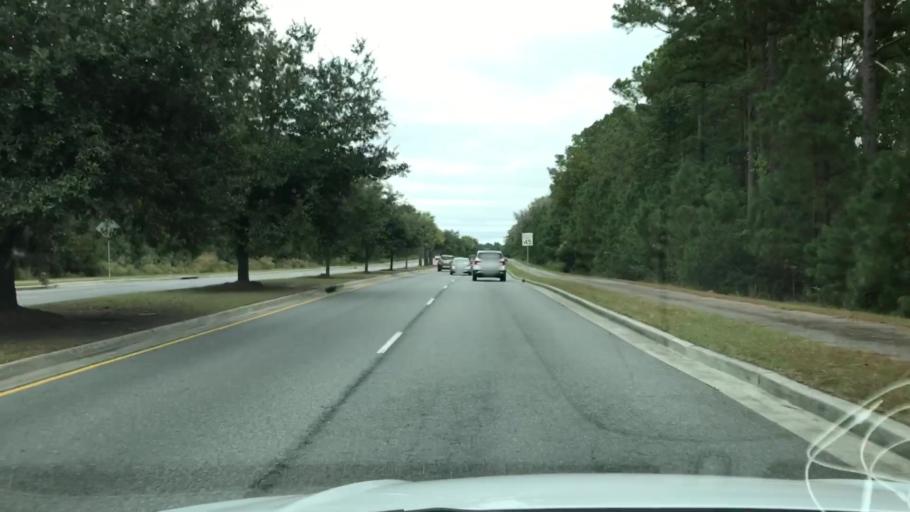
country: US
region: South Carolina
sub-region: Beaufort County
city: Bluffton
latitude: 32.2578
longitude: -80.8911
